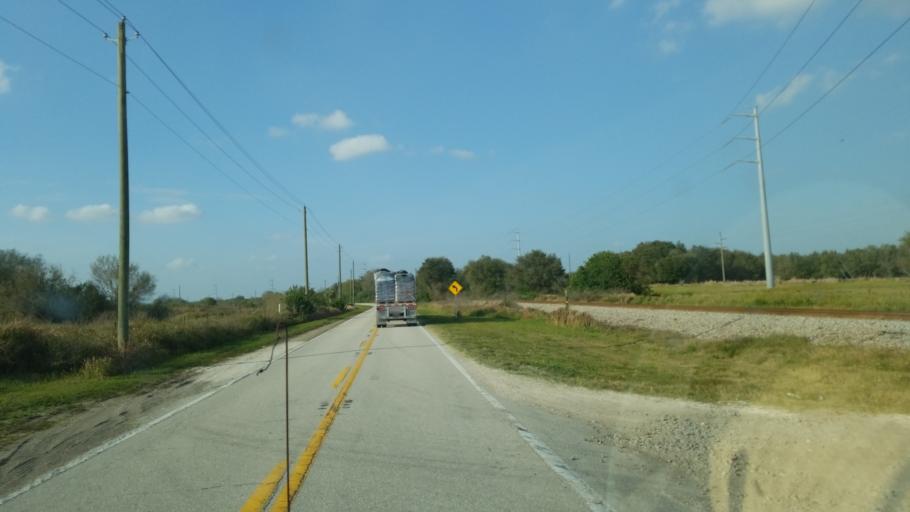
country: US
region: Florida
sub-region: Hardee County
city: Bowling Green
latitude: 27.7181
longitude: -81.9615
